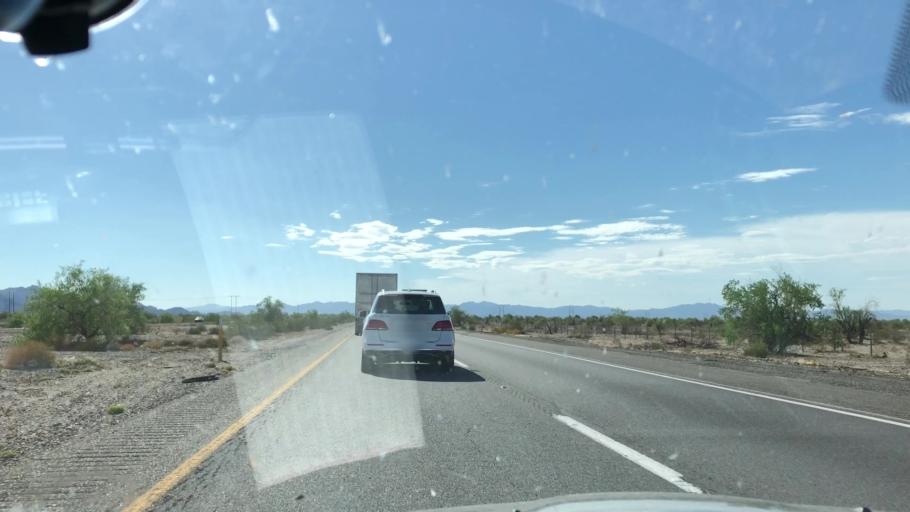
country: US
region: California
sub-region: Riverside County
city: Mesa Verde
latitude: 33.6744
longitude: -115.2159
